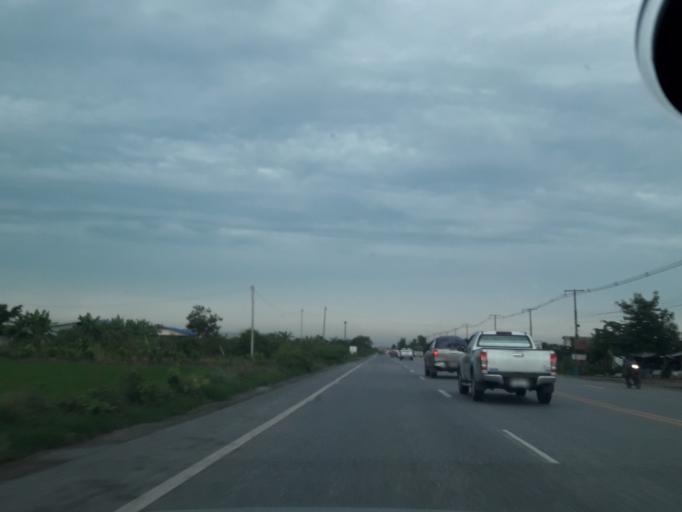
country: TH
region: Pathum Thani
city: Nong Suea
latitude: 14.1513
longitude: 100.7474
